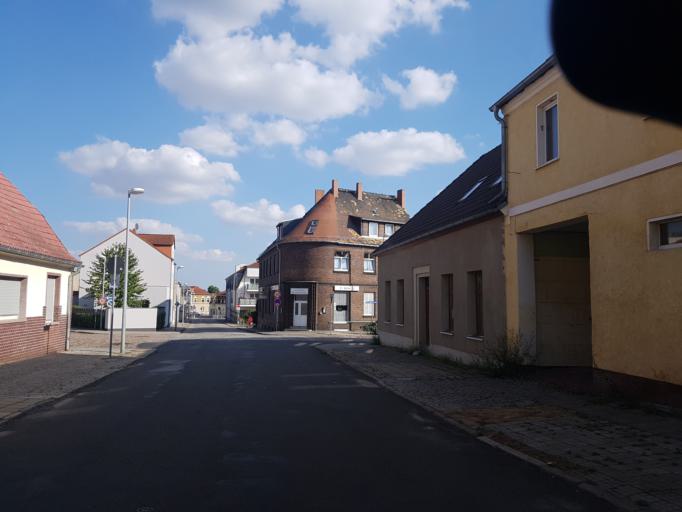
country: DE
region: Saxony-Anhalt
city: Coswig
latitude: 51.8870
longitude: 12.4491
